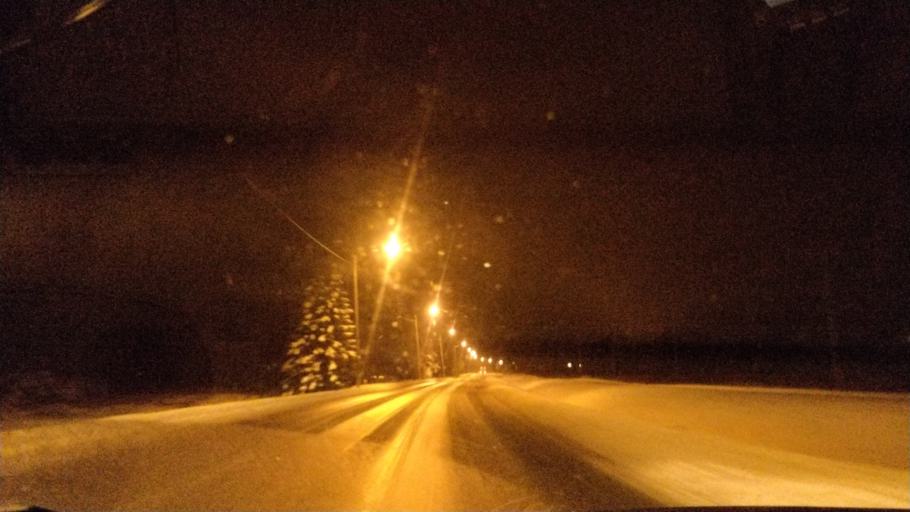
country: FI
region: Lapland
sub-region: Rovaniemi
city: Rovaniemi
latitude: 66.3156
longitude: 25.3619
